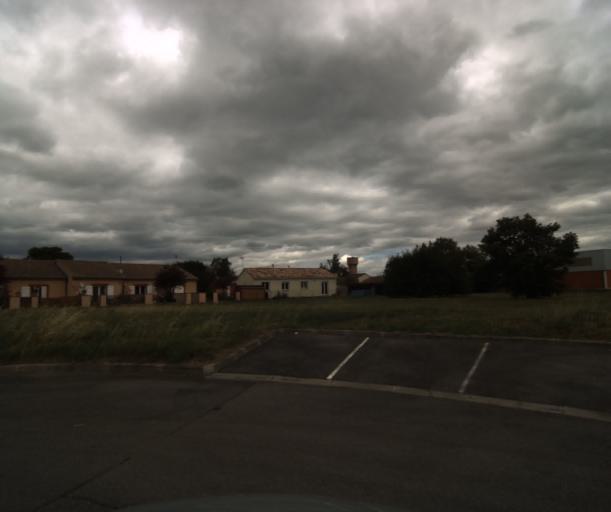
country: FR
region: Midi-Pyrenees
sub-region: Departement de la Haute-Garonne
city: Roquettes
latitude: 43.4760
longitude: 1.3787
